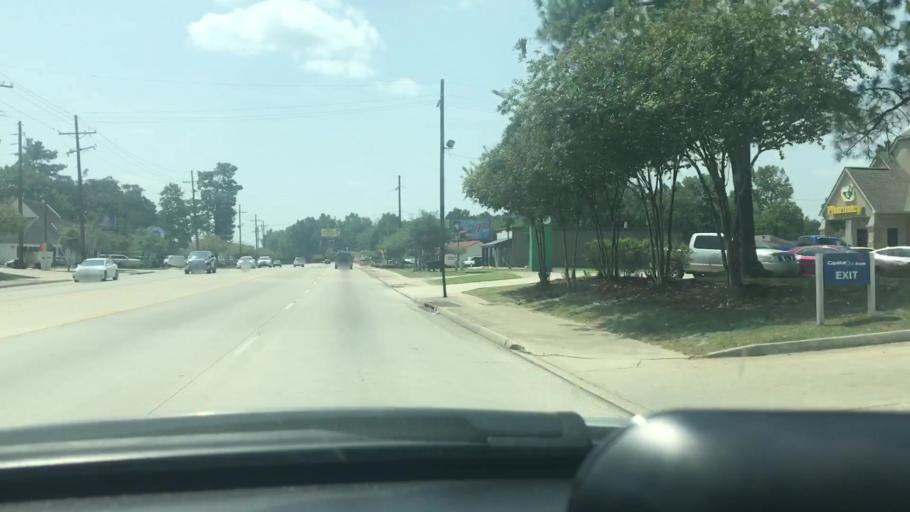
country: US
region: Louisiana
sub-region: Livingston Parish
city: Walker
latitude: 30.4861
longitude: -90.8623
